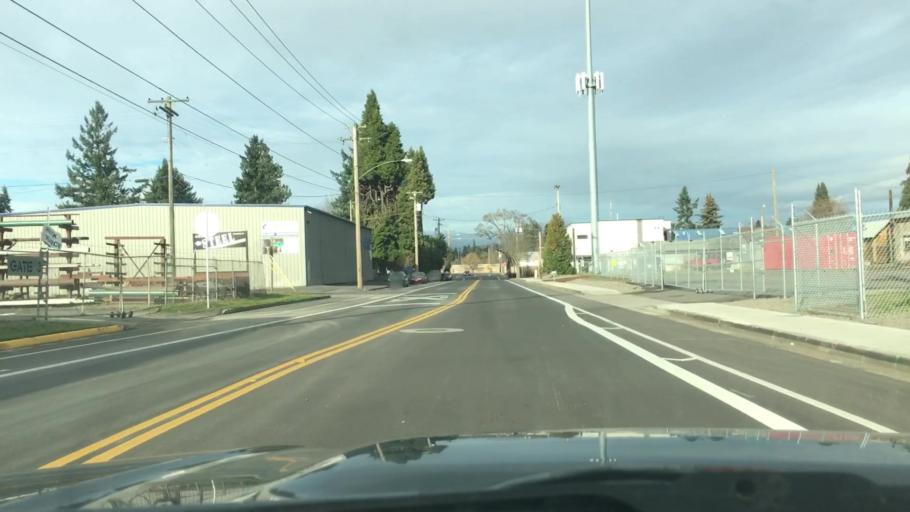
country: US
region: Oregon
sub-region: Lane County
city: Eugene
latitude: 44.0609
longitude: -123.1226
